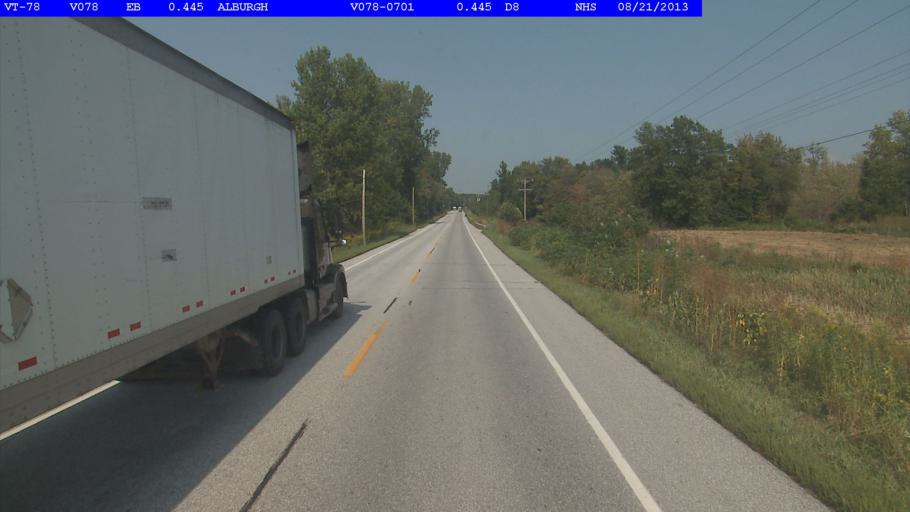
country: US
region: New York
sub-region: Clinton County
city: Rouses Point
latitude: 44.9651
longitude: -73.2718
